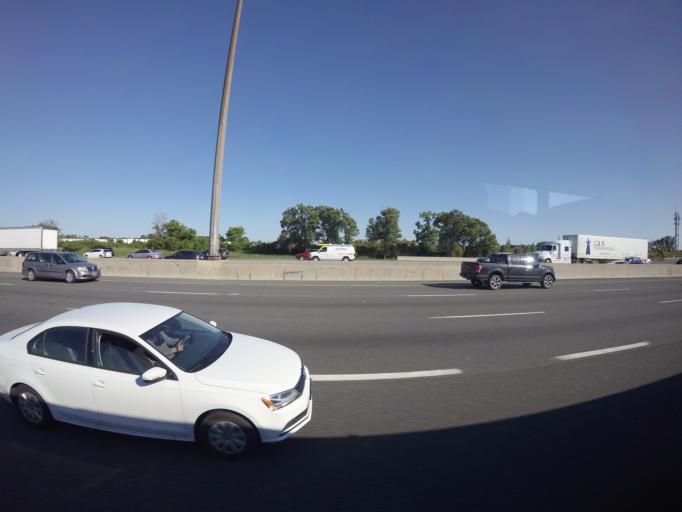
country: CA
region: Ontario
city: Ajax
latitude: 43.8409
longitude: -79.0667
